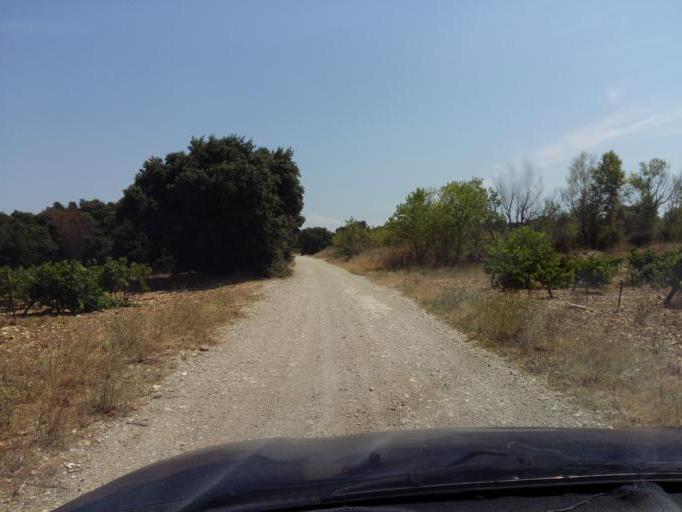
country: FR
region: Provence-Alpes-Cote d'Azur
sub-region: Departement du Vaucluse
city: Camaret-sur-Aigues
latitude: 44.1780
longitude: 4.8606
